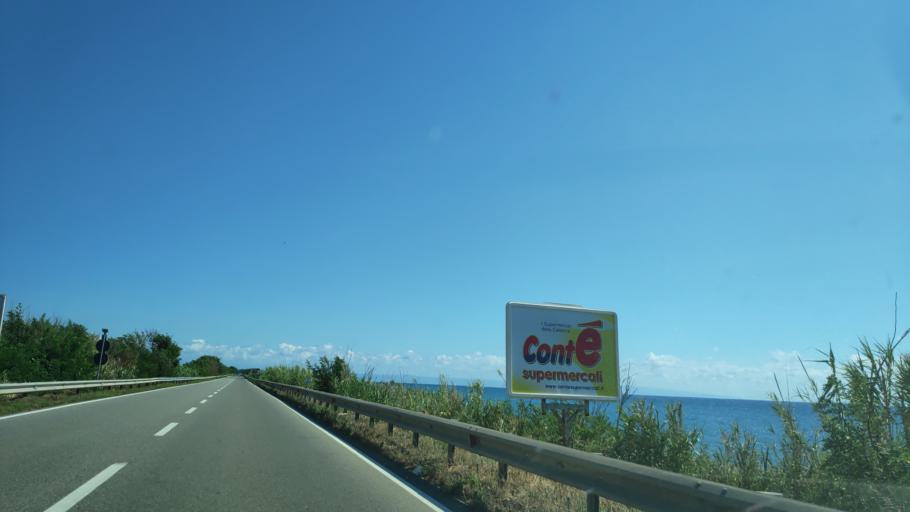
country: IT
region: Calabria
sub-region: Provincia di Cosenza
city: Campora San Giovanni
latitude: 39.0450
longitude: 16.0978
